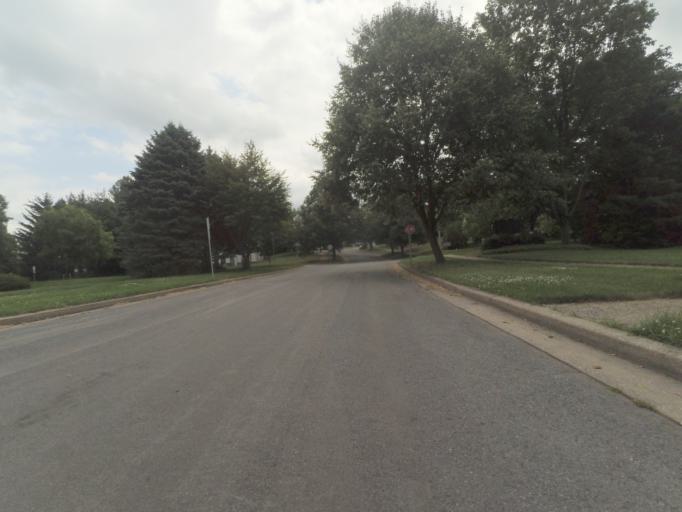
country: US
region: Pennsylvania
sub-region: Centre County
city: State College
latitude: 40.7736
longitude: -77.8622
